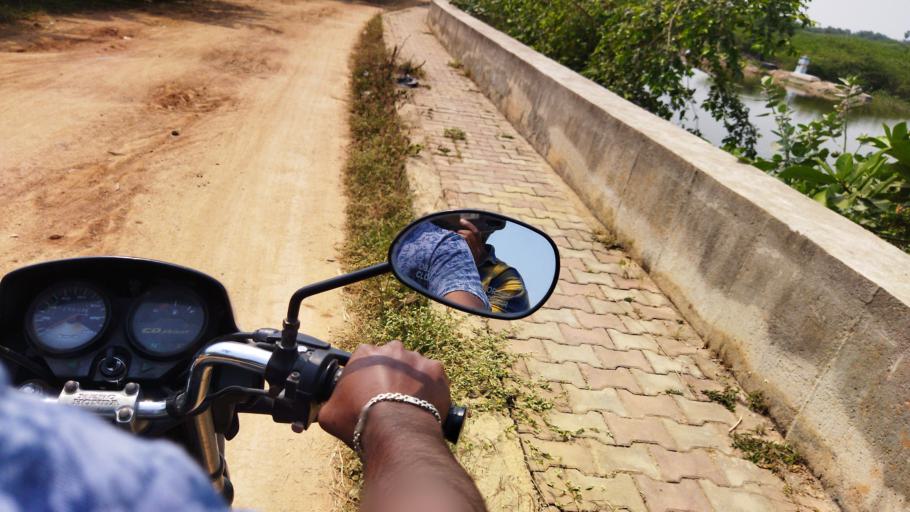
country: IN
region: Telangana
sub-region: Nalgonda
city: Nalgonda
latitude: 17.1616
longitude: 79.4183
